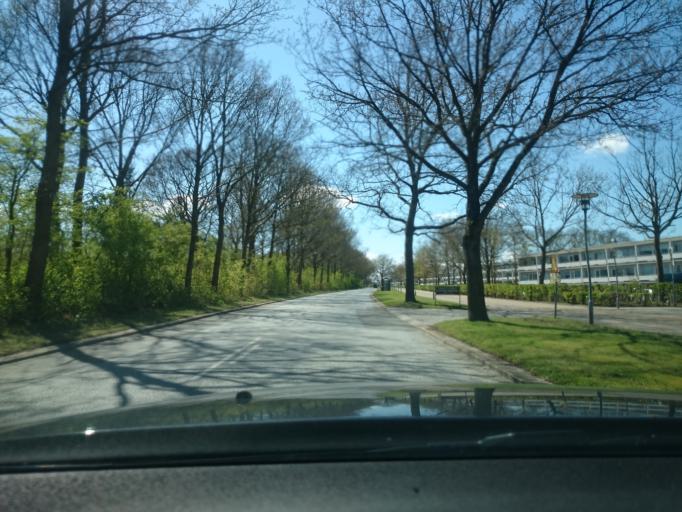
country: DK
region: Capital Region
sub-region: Lyngby-Tarbaek Kommune
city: Kongens Lyngby
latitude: 55.7946
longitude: 12.5361
